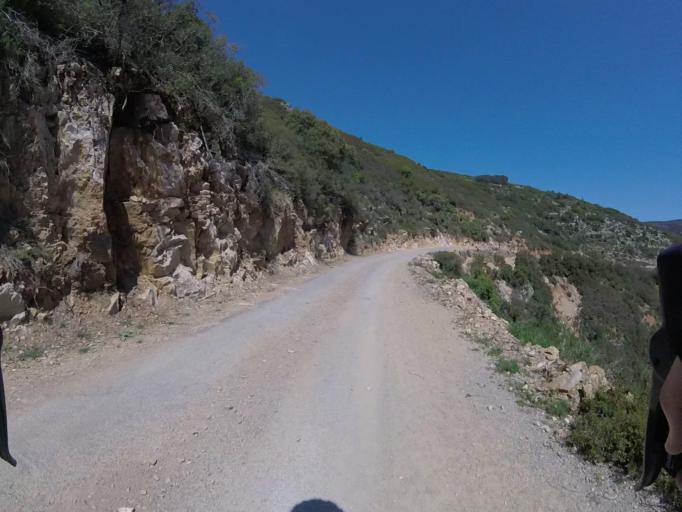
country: ES
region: Valencia
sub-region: Provincia de Castello
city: Sierra-Engarceran
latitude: 40.2516
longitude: -0.0267
